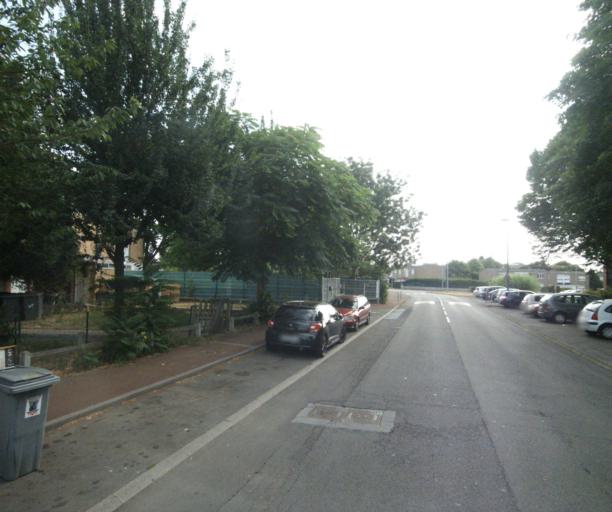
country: FR
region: Nord-Pas-de-Calais
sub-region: Departement du Nord
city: Tourcoing
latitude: 50.7387
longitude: 3.1768
